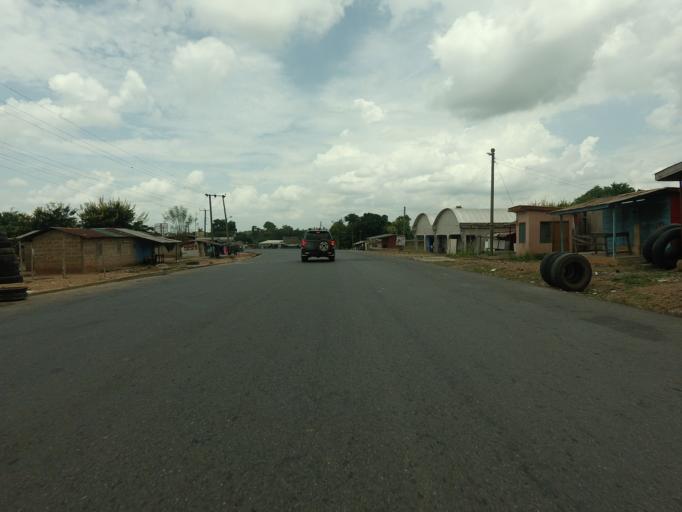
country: GH
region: Volta
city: Ho
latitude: 6.4171
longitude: 0.1723
